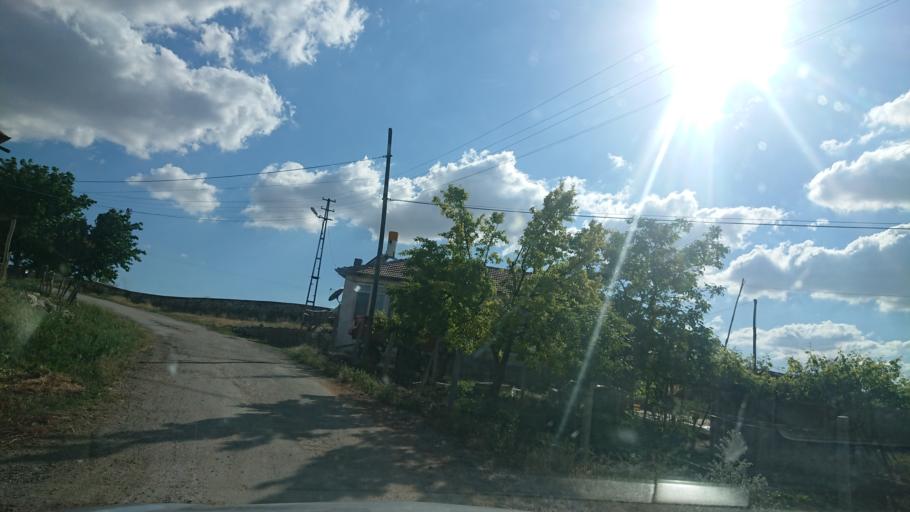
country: TR
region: Aksaray
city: Agacoren
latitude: 38.7537
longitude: 33.8855
